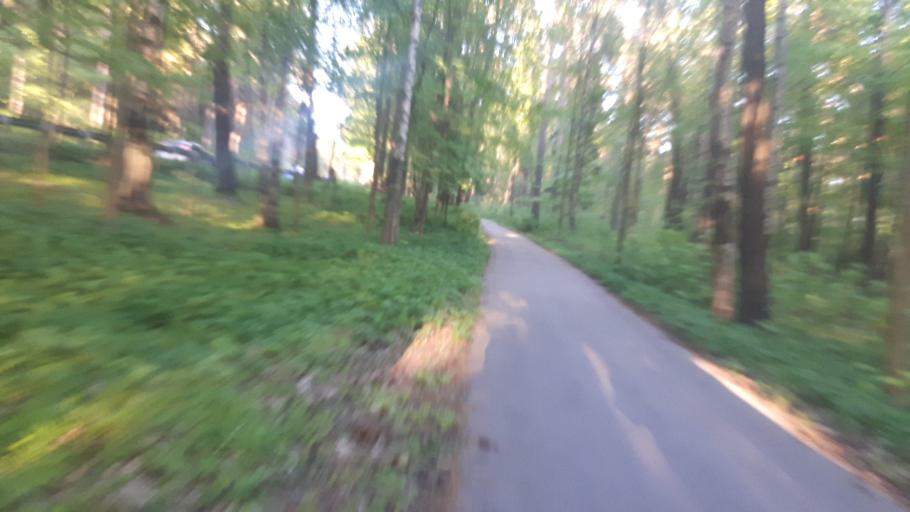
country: RU
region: Leningrad
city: Roshchino
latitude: 60.1937
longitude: 29.6265
